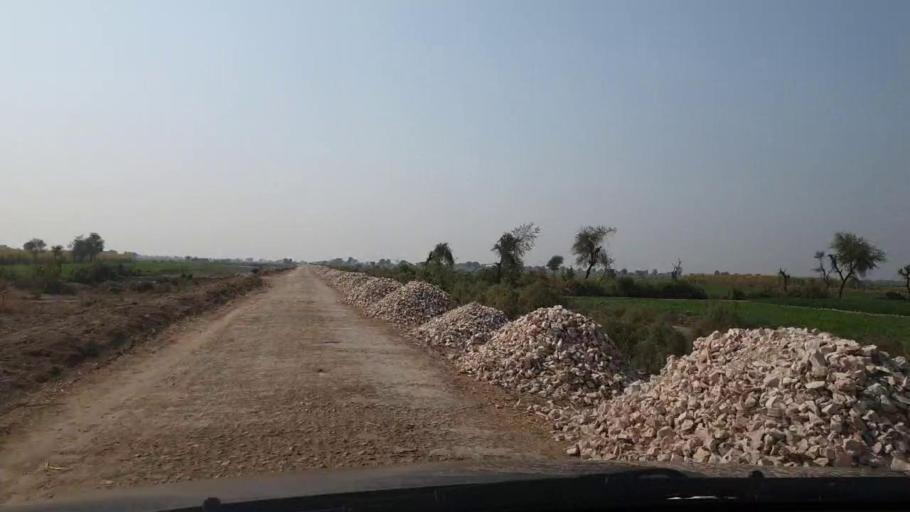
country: PK
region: Sindh
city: Jhol
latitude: 25.8953
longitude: 69.0059
